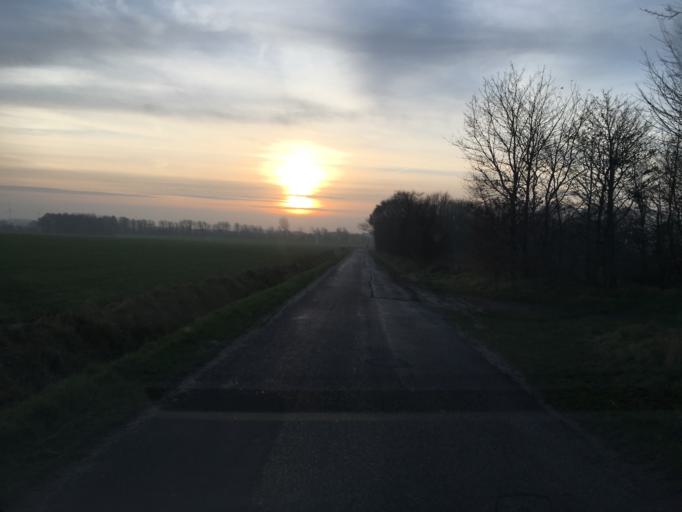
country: DK
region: South Denmark
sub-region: Tonder Kommune
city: Toftlund
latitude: 55.1406
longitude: 9.0338
